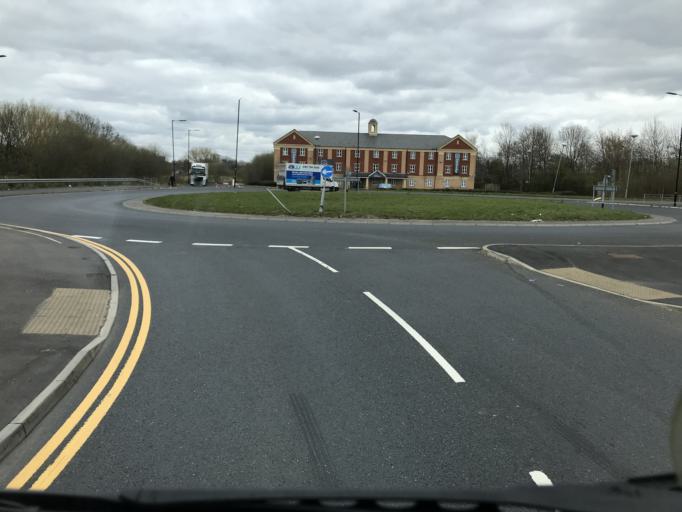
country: GB
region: England
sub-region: Trafford
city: Urmston
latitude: 53.4702
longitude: -2.3641
